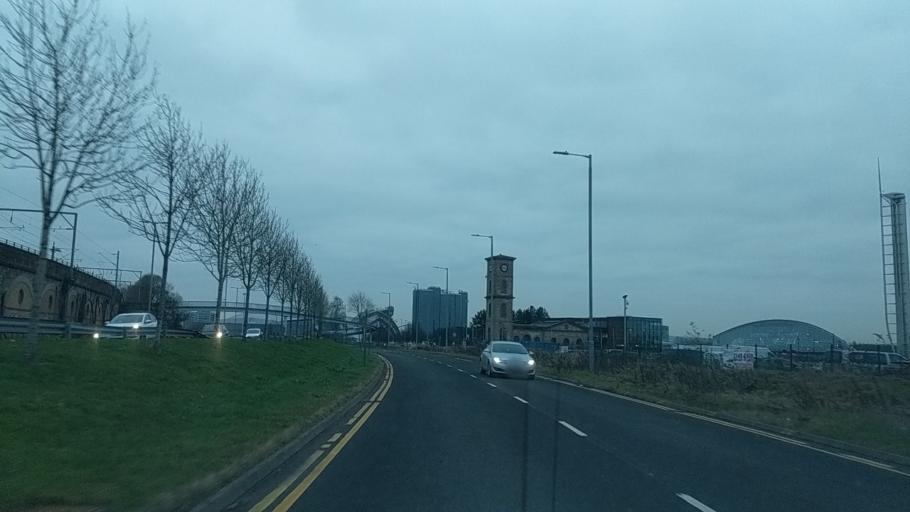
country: GB
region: Scotland
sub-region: Glasgow City
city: Glasgow
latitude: 55.8637
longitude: -4.2990
